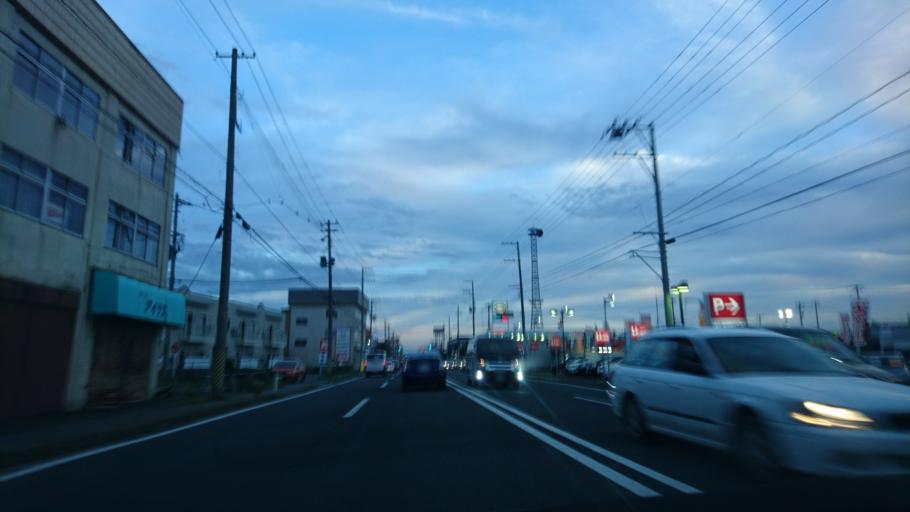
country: JP
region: Iwate
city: Morioka-shi
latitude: 39.6705
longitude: 141.1564
